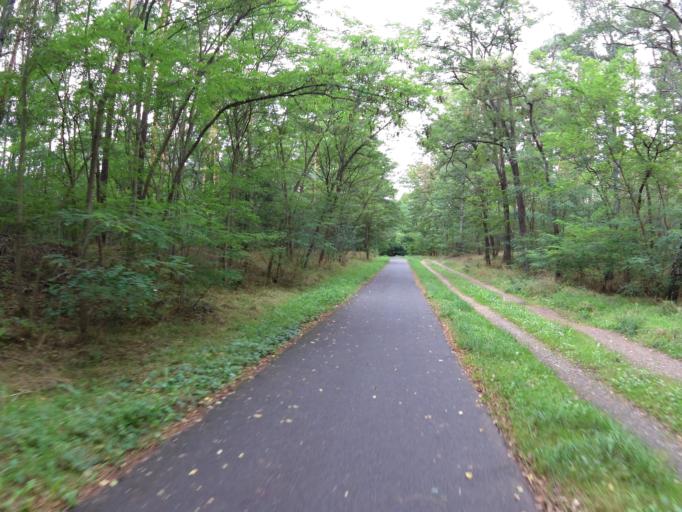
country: DE
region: Brandenburg
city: Reichenwalde
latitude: 52.2403
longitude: 13.9825
